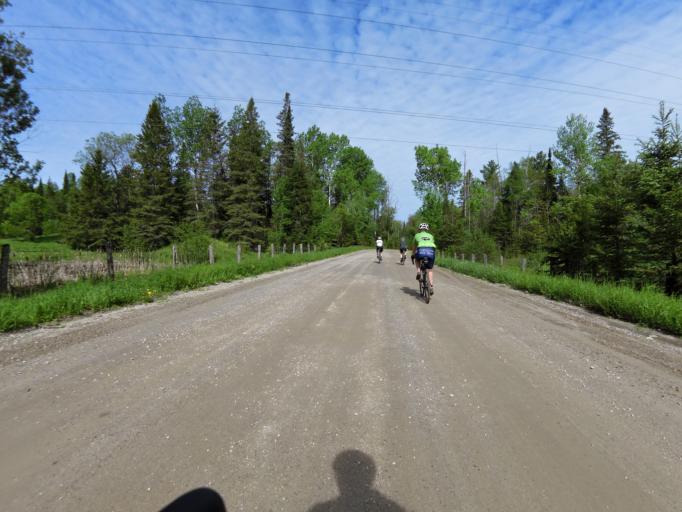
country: CA
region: Quebec
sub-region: Outaouais
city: Wakefield
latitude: 45.6953
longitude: -75.8917
